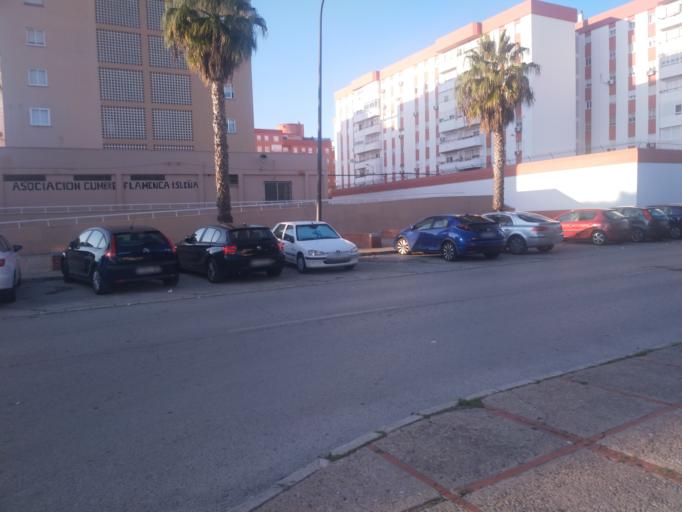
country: ES
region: Andalusia
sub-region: Provincia de Cadiz
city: San Fernando
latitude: 36.4605
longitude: -6.2029
